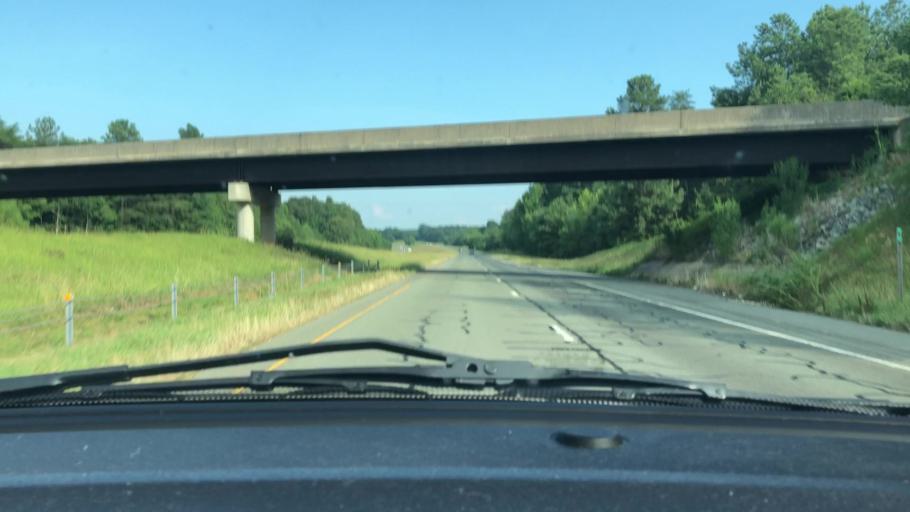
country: US
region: North Carolina
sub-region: Randolph County
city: Liberty
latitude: 35.7979
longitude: -79.5354
